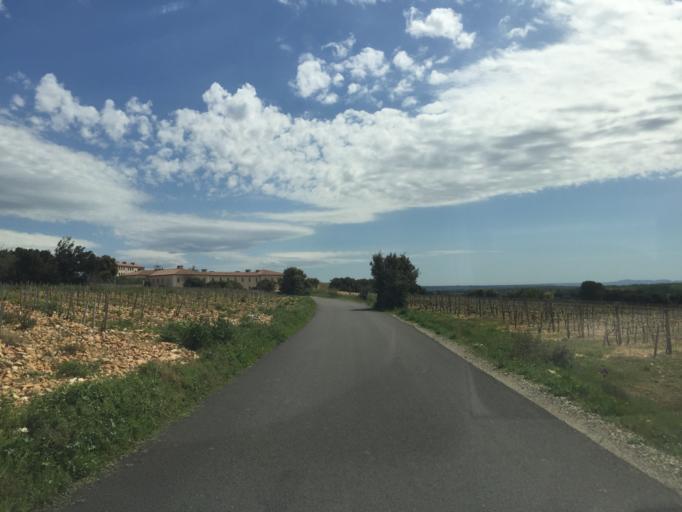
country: FR
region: Provence-Alpes-Cote d'Azur
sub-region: Departement du Vaucluse
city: Chateauneuf-du-Pape
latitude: 44.0547
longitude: 4.8194
